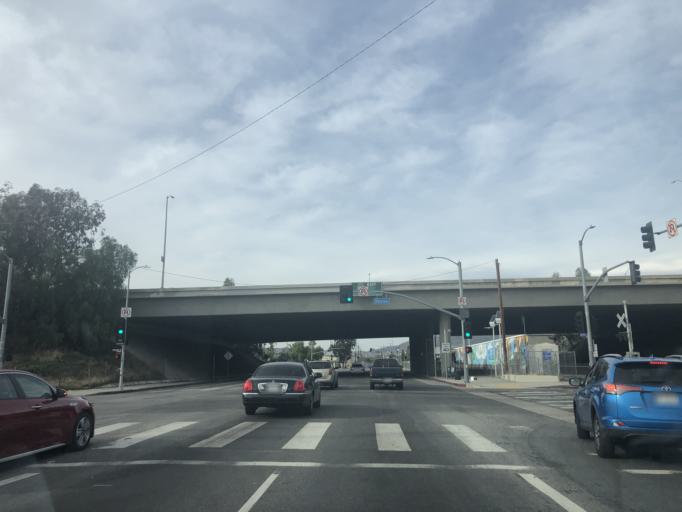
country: US
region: California
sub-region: Los Angeles County
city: San Fernando
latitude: 34.2718
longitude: -118.4282
